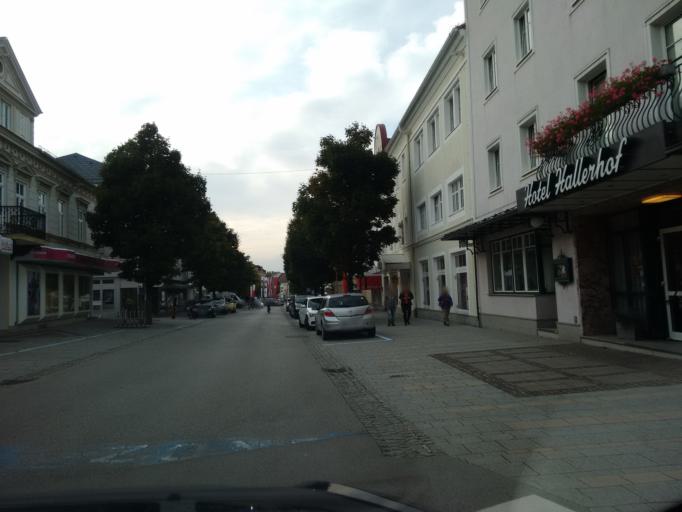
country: AT
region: Upper Austria
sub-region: Politischer Bezirk Steyr-Land
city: Bad Hall
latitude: 48.0339
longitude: 14.2107
